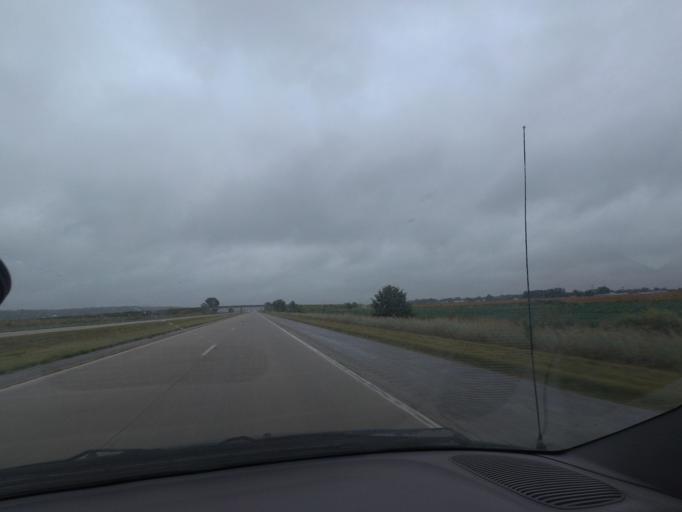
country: US
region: Illinois
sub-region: Adams County
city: Payson
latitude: 39.7214
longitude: -91.2176
